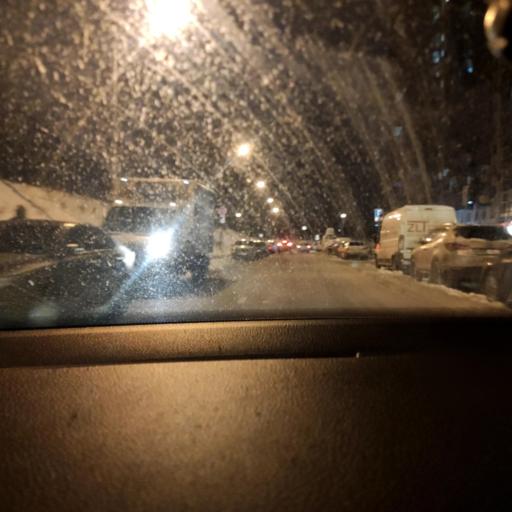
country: RU
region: Moskovskaya
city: Pavshino
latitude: 55.8639
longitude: 37.3719
